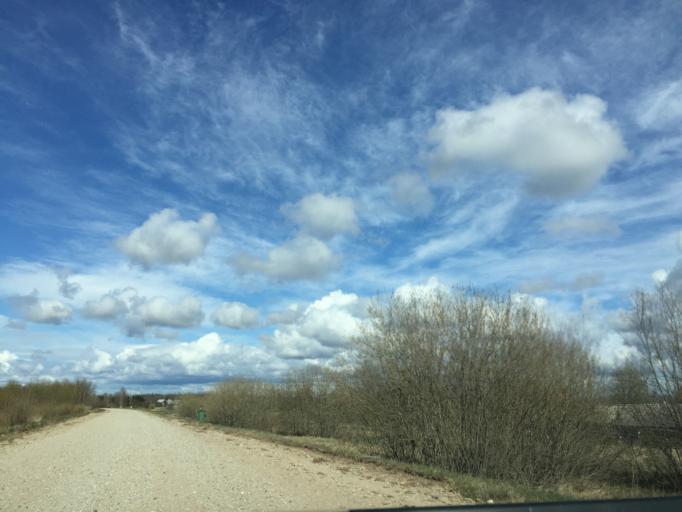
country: LV
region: Limbazu Rajons
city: Limbazi
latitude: 57.5620
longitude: 24.5903
